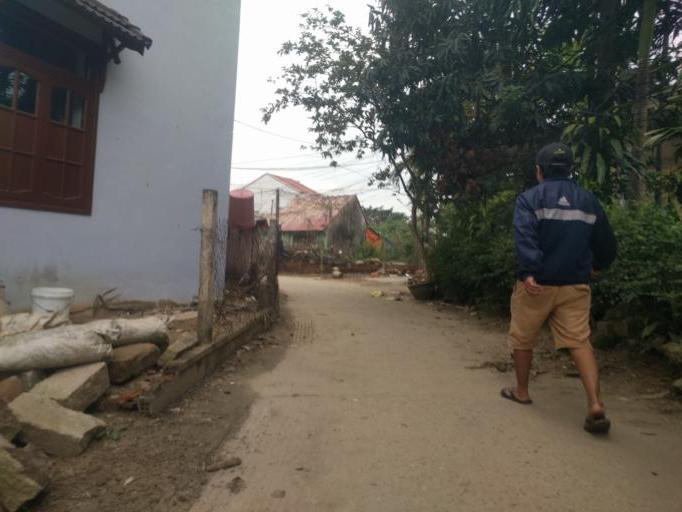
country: VN
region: Quang Nam
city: Hoi An
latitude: 15.8734
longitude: 108.3305
